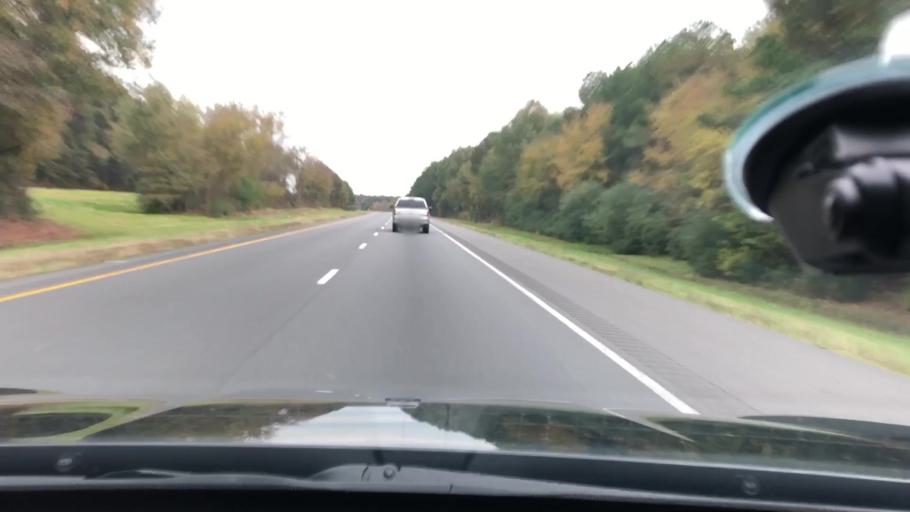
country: US
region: Arkansas
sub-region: Hempstead County
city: Hope
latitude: 33.7317
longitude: -93.5325
